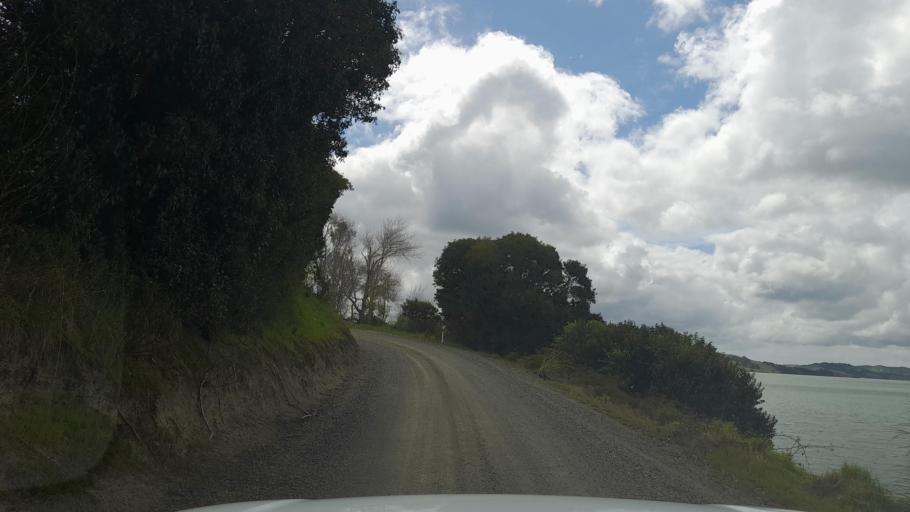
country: NZ
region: Auckland
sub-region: Auckland
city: Wellsford
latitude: -36.2203
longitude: 174.3207
